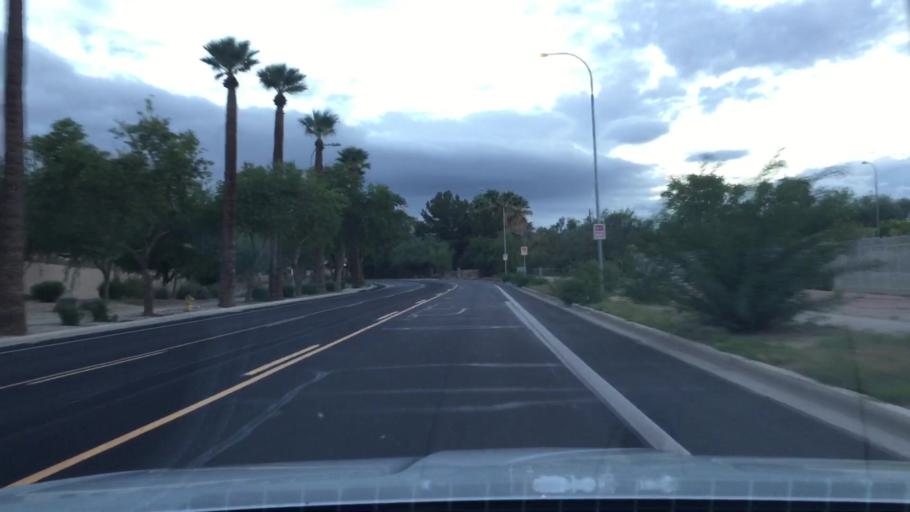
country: US
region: Arizona
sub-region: Maricopa County
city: Phoenix
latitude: 33.3757
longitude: -112.0480
